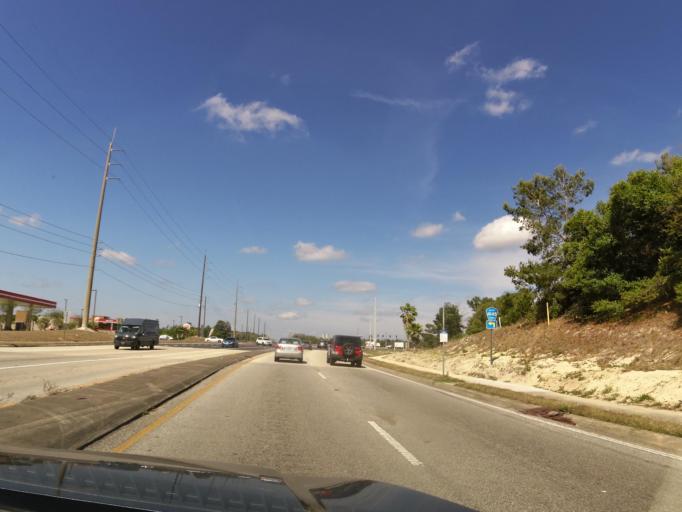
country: US
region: Florida
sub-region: Volusia County
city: Lake Helen
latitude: 28.9486
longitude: -81.2489
